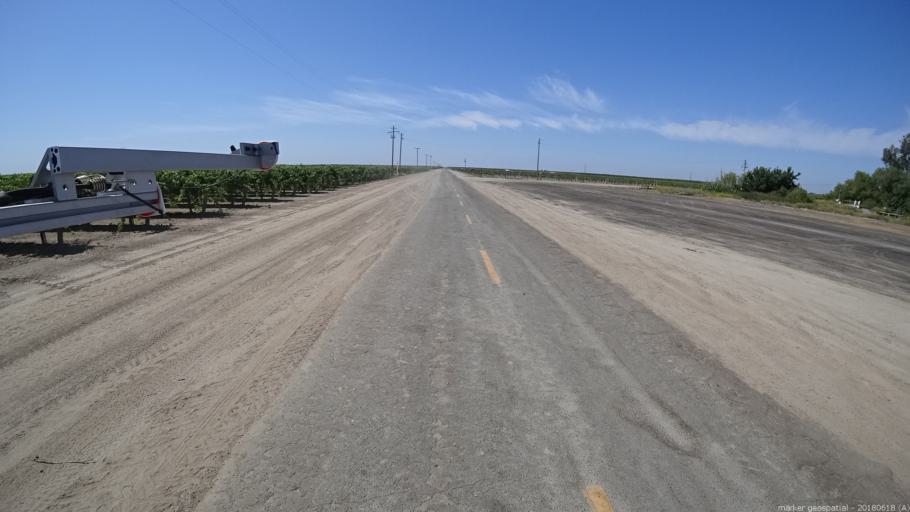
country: US
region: California
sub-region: Madera County
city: Parkwood
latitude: 36.8681
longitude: -120.1830
